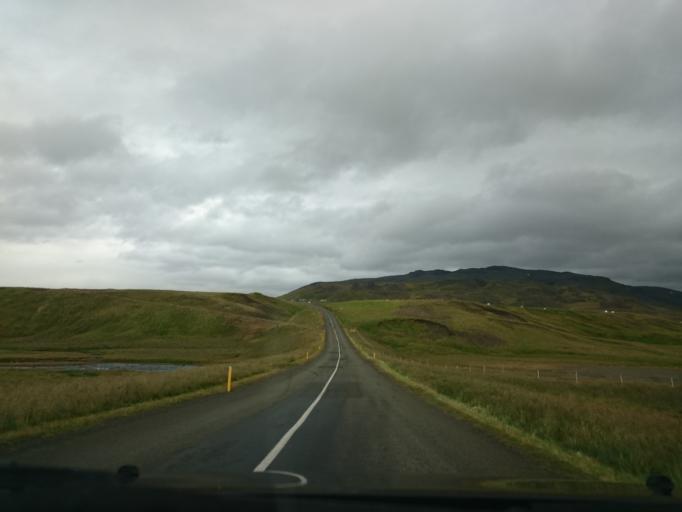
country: IS
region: West
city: Stykkisholmur
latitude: 65.4700
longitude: -21.9159
